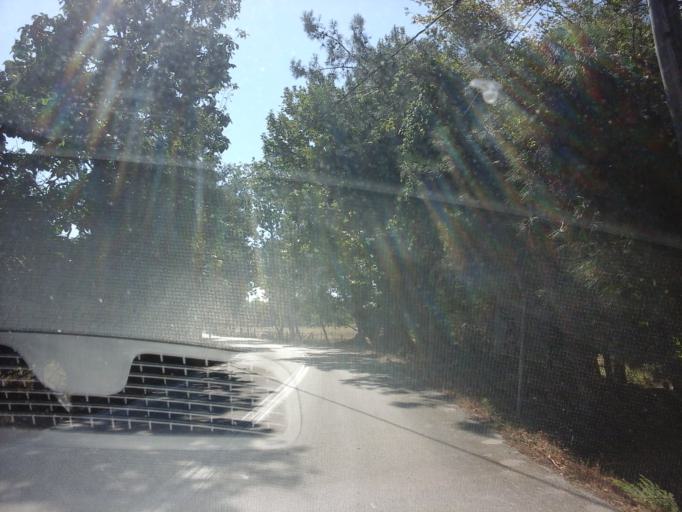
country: GR
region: East Macedonia and Thrace
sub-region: Nomos Evrou
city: Samothraki
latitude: 40.4921
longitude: 25.6408
